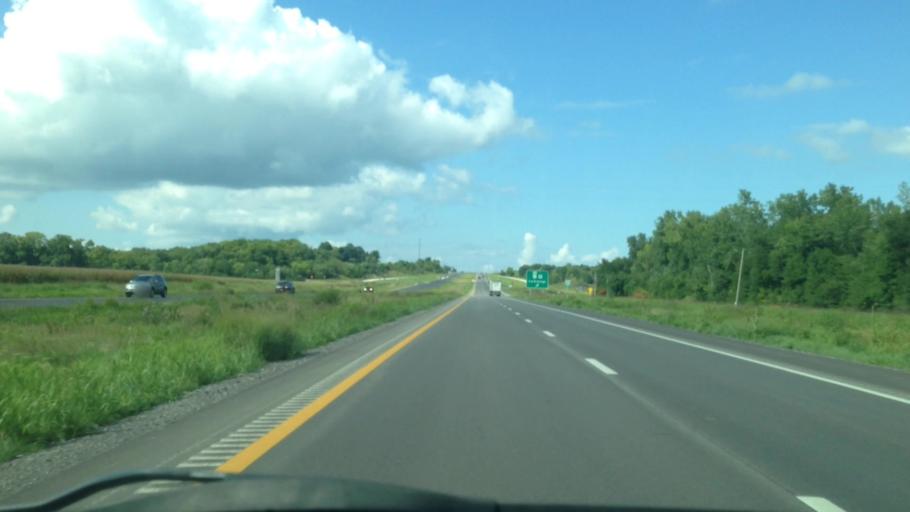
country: US
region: Illinois
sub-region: Adams County
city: Quincy
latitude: 40.0041
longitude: -91.5264
